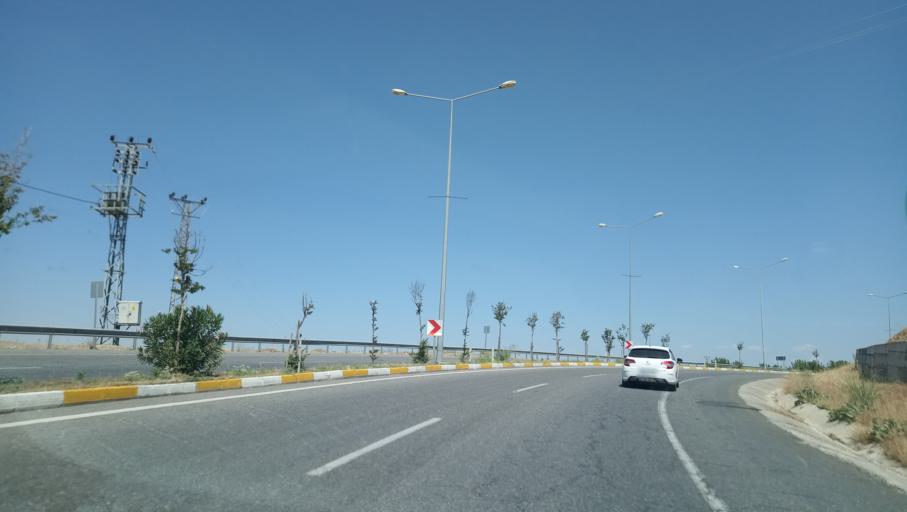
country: TR
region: Siirt
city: Civankan
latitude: 37.9499
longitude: 41.8627
